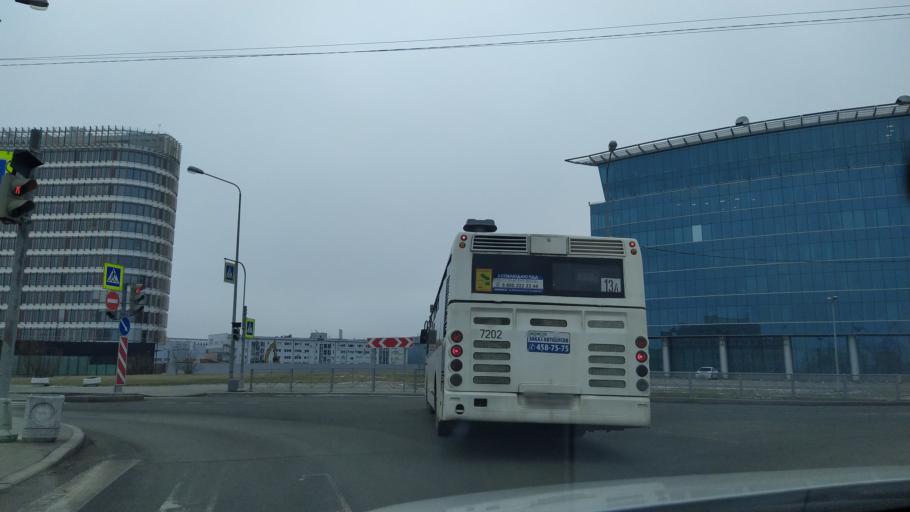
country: RU
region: St.-Petersburg
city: Kupchino
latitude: 59.8086
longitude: 30.3140
